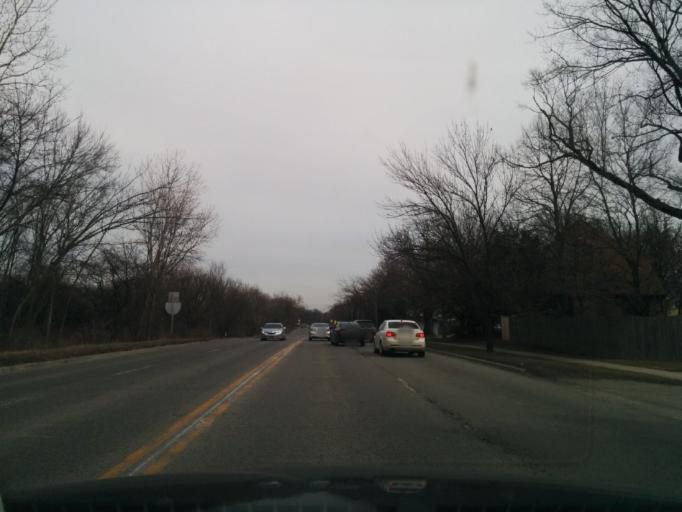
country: US
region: Illinois
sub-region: Cook County
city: Western Springs
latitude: 41.8197
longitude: -87.9069
